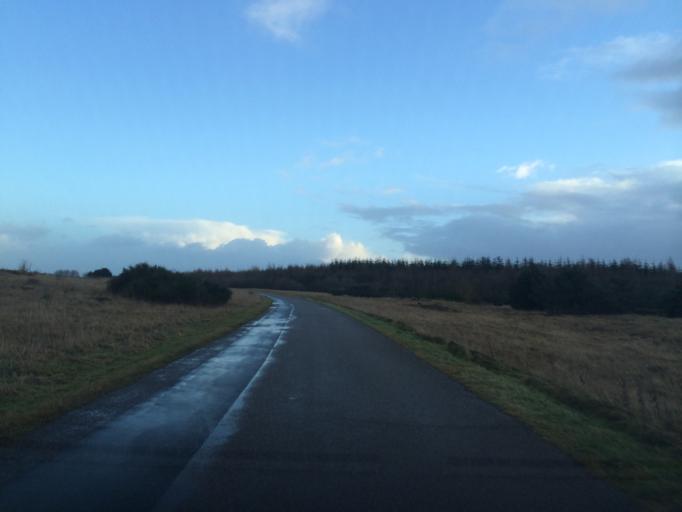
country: DK
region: Central Jutland
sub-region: Holstebro Kommune
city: Ulfborg
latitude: 56.2420
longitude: 8.3922
